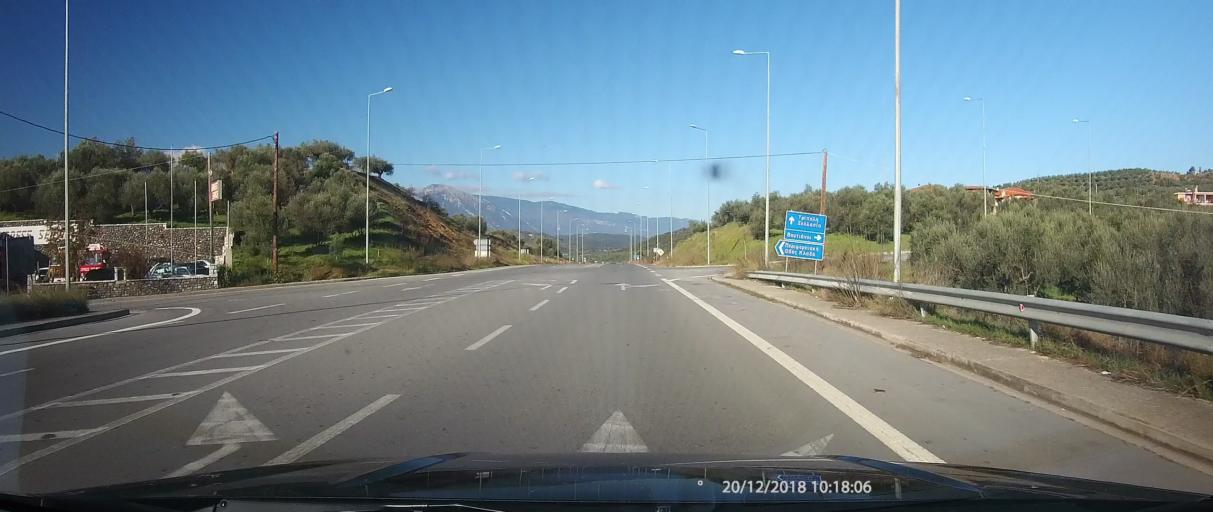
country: GR
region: Peloponnese
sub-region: Nomos Lakonias
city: Sparti
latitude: 37.1134
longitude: 22.4304
